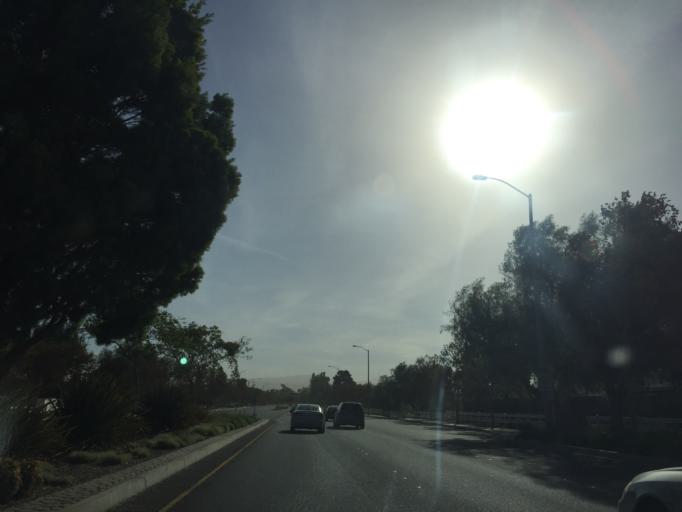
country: US
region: California
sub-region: Orange County
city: Yorba Linda
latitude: 33.8974
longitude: -117.8272
